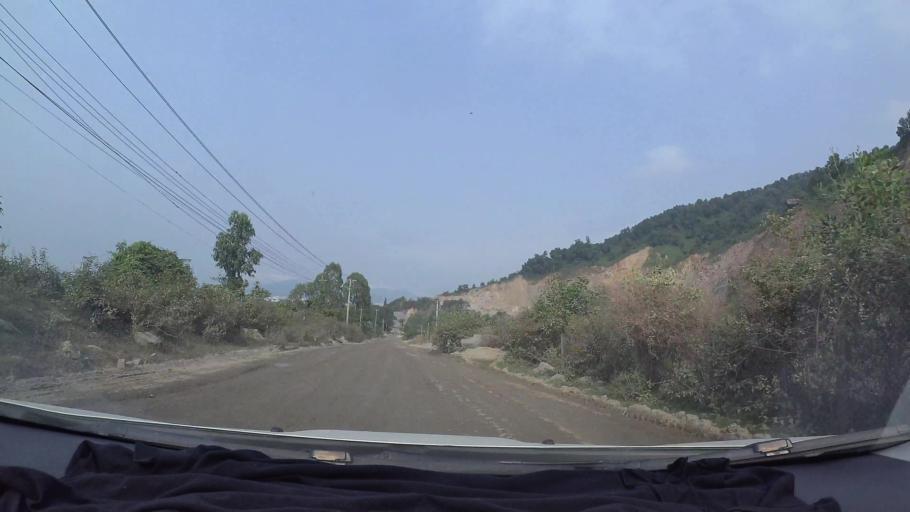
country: VN
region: Da Nang
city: Lien Chieu
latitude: 16.0379
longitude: 108.1558
